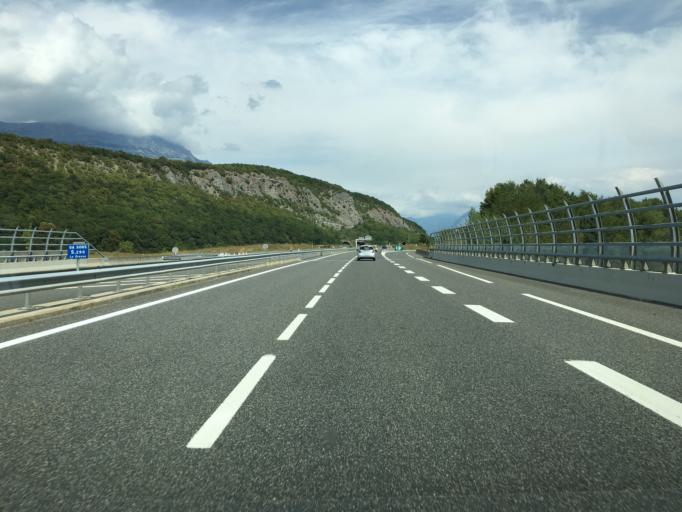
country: FR
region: Rhone-Alpes
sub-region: Departement de l'Isere
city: Vif
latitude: 45.0731
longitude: 5.6797
